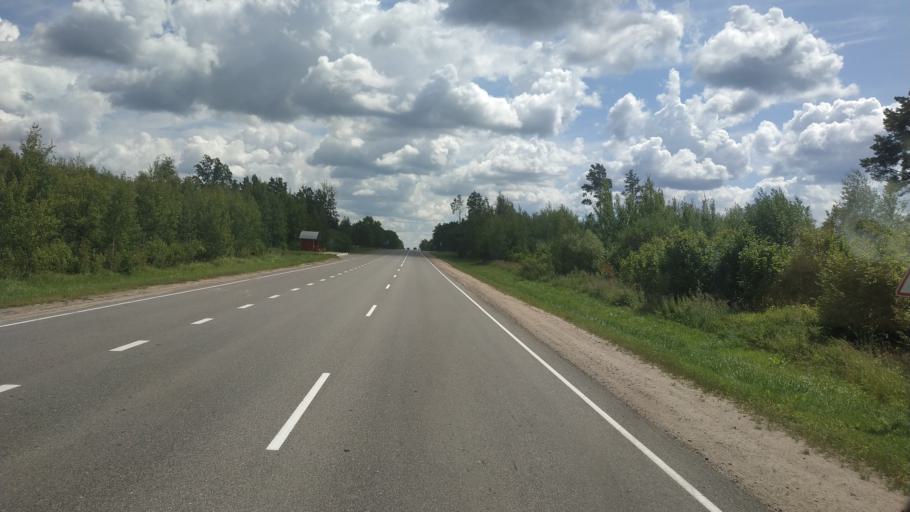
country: BY
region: Mogilev
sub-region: Mahilyowski Rayon
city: Veyno
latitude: 53.8219
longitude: 30.4312
